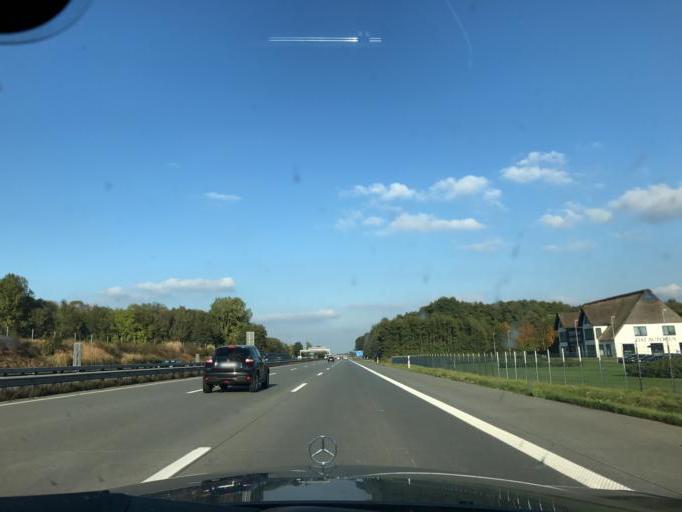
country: DE
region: Lower Saxony
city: Gyhum
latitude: 53.1963
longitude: 9.2894
